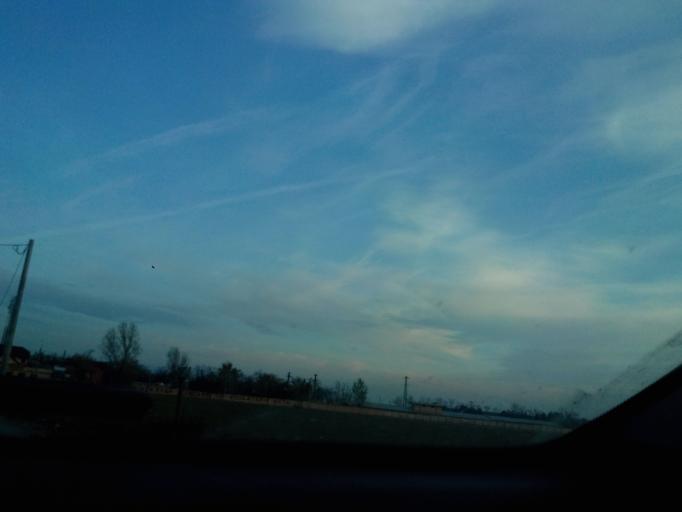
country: RO
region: Prahova
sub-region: Oras Baicoi
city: Tufeni
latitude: 45.0347
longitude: 25.8170
